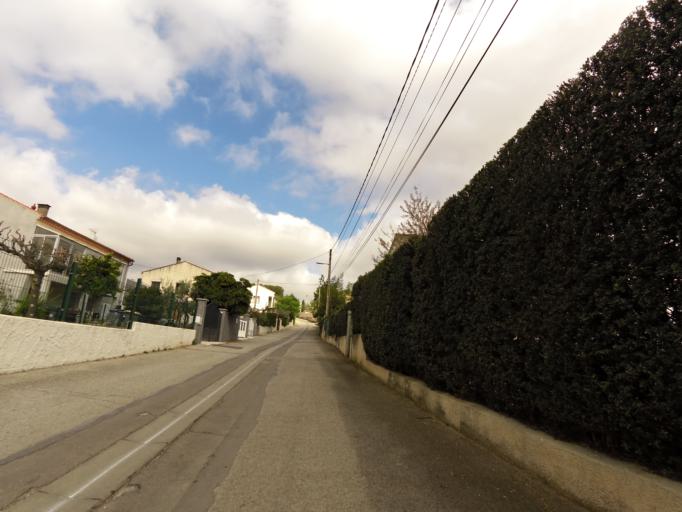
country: FR
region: Languedoc-Roussillon
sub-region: Departement du Gard
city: Vergeze
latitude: 43.7459
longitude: 4.2250
